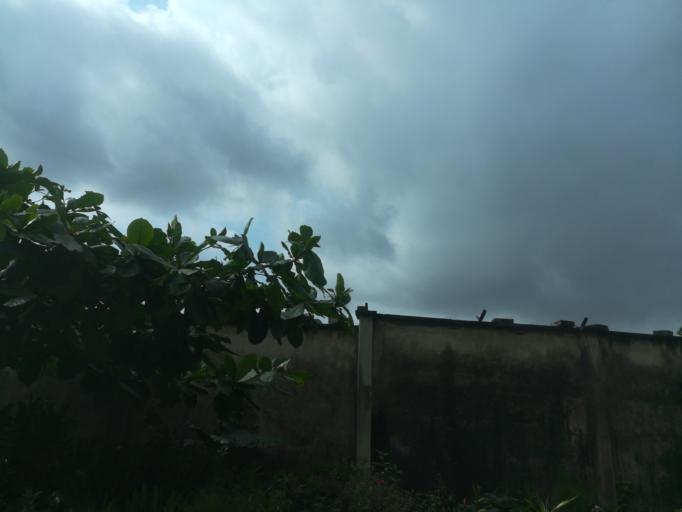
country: NG
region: Lagos
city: Oshodi
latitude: 6.5779
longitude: 3.3570
